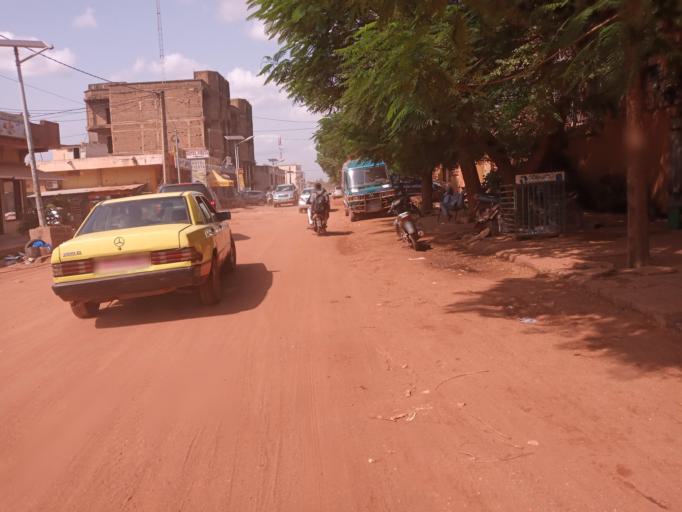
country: ML
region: Bamako
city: Bamako
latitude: 12.5829
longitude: -7.9538
